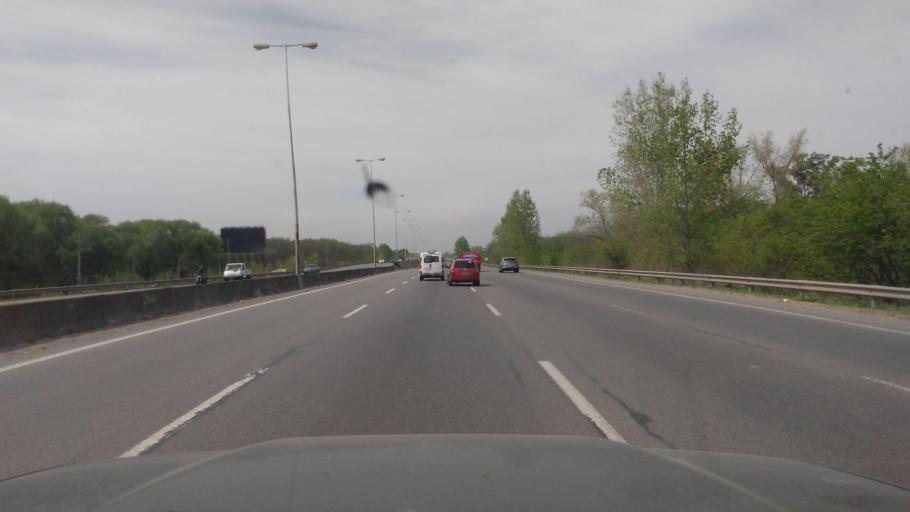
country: AR
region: Buenos Aires
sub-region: Partido de Pilar
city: Pilar
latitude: -34.4438
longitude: -58.9608
